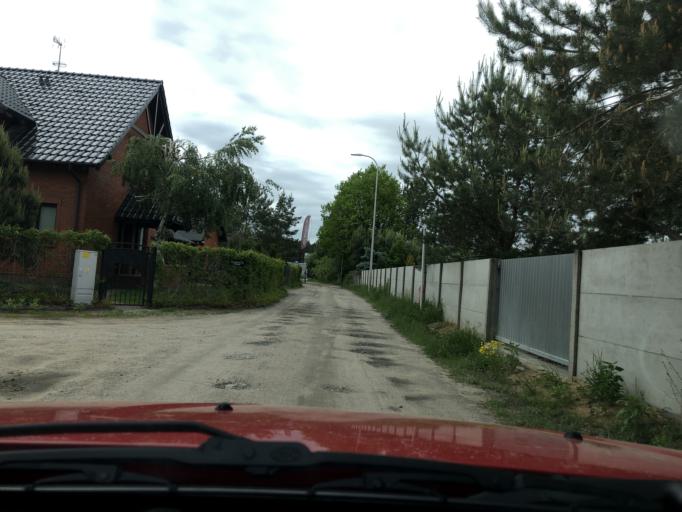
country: PL
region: Greater Poland Voivodeship
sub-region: Powiat poznanski
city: Baranowo
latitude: 52.4056
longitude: 16.7355
